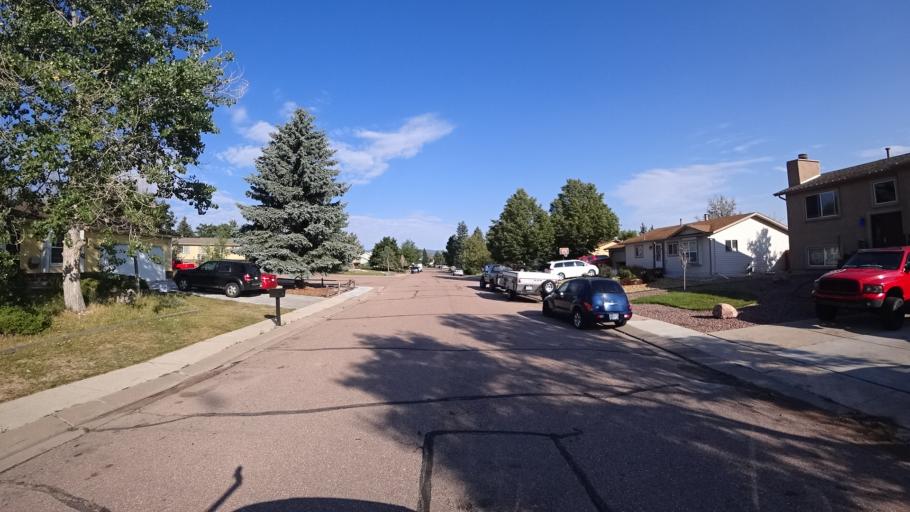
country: US
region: Colorado
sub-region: El Paso County
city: Black Forest
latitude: 38.9447
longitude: -104.7654
